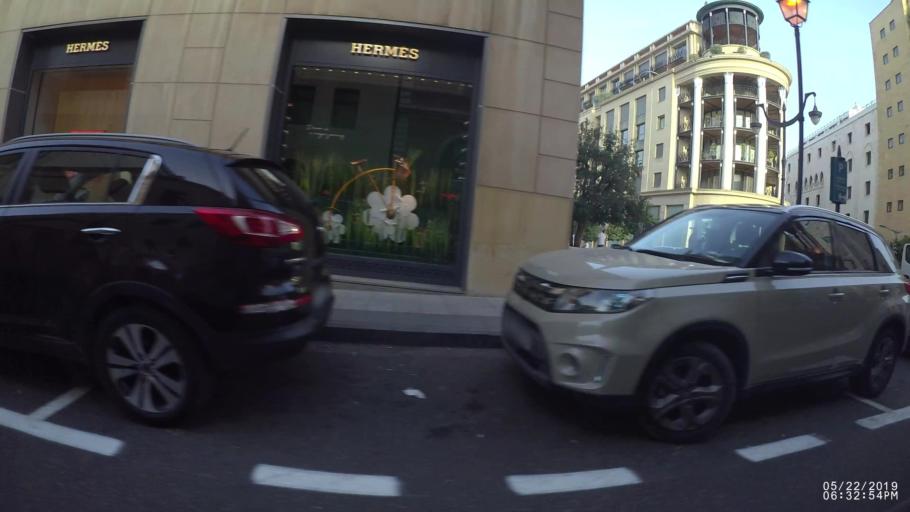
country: LB
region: Beyrouth
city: Beirut
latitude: 33.8989
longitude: 35.5027
